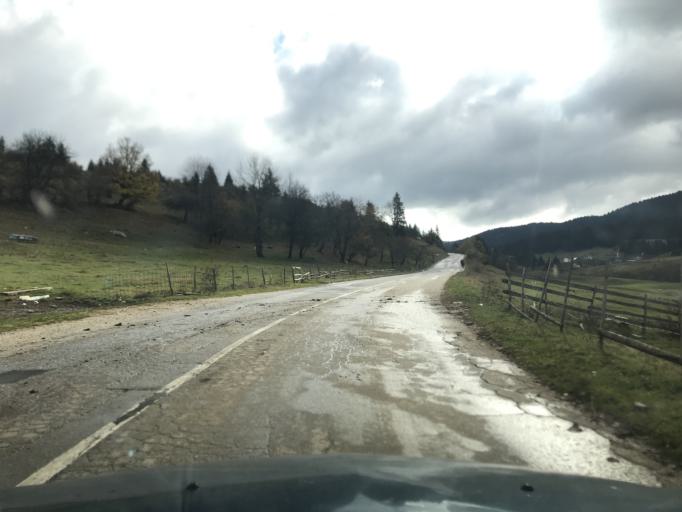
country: BA
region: Federation of Bosnia and Herzegovina
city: Turbe
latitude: 44.3149
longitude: 17.5283
